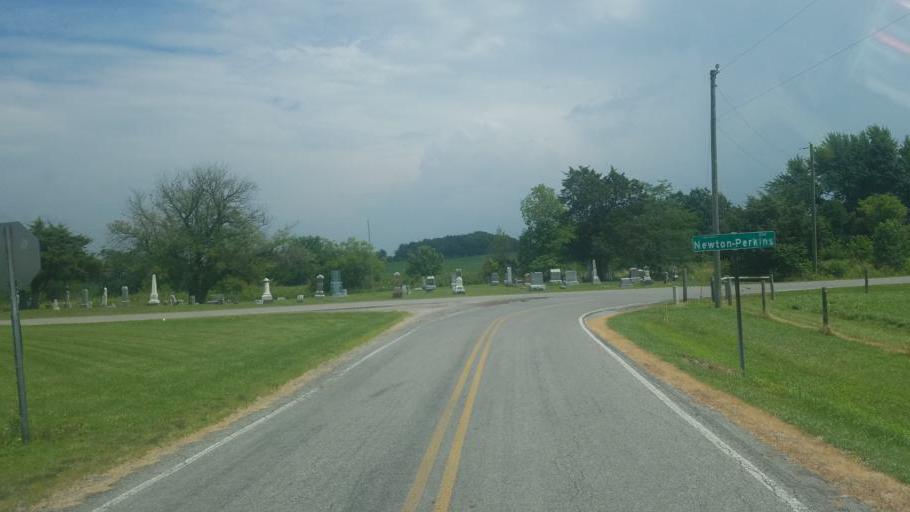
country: US
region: Ohio
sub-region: Champaign County
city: North Lewisburg
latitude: 40.3982
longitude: -83.5203
